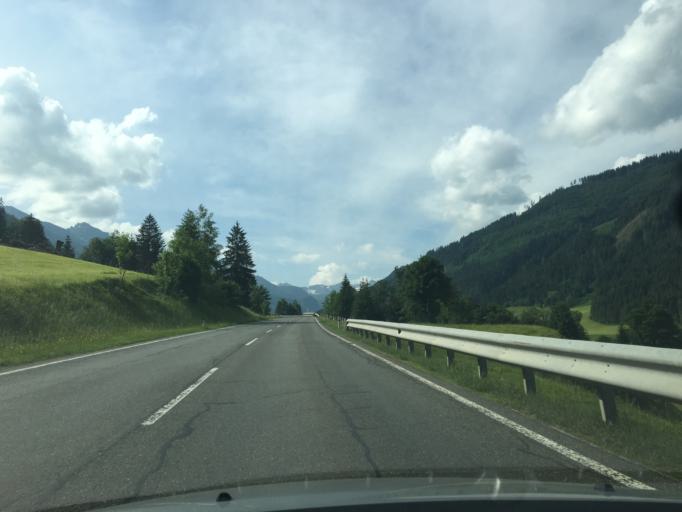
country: AT
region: Salzburg
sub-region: Politischer Bezirk Sankt Johann im Pongau
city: Forstau
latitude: 47.3570
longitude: 13.4971
